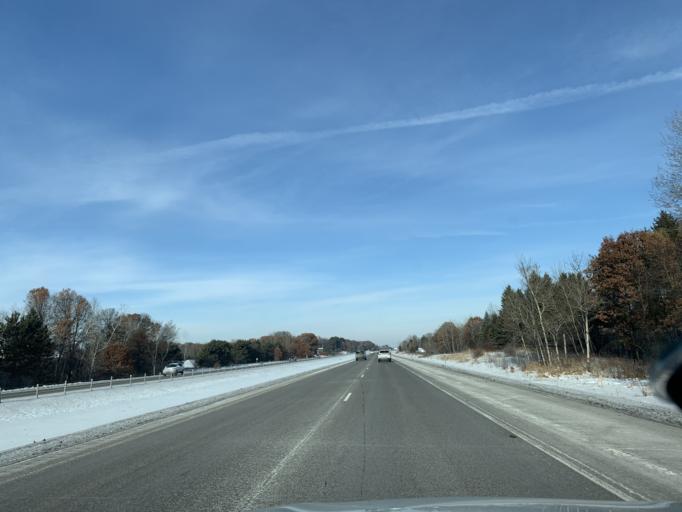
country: US
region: Minnesota
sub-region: Chisago County
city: Wyoming
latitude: 45.3070
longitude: -93.0029
